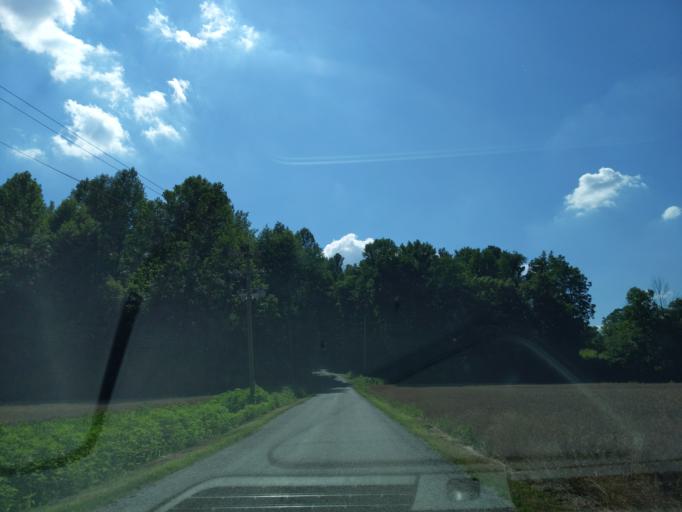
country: US
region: Indiana
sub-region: Ripley County
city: Osgood
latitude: 39.1903
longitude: -85.4100
